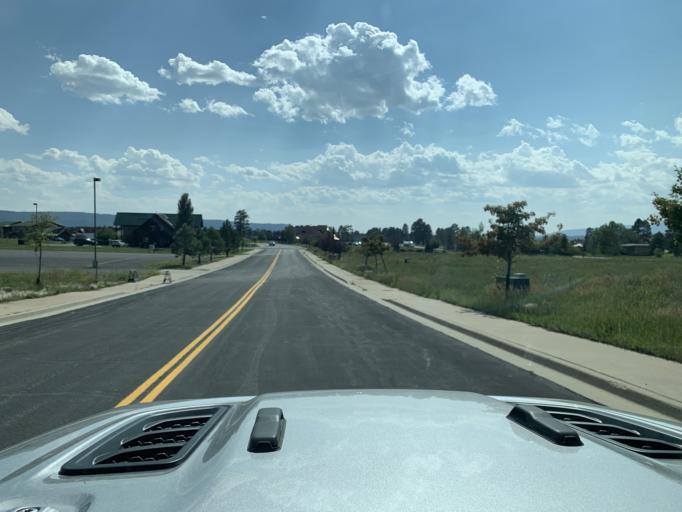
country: US
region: Colorado
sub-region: Archuleta County
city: Pagosa Springs
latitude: 37.2653
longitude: -107.0559
